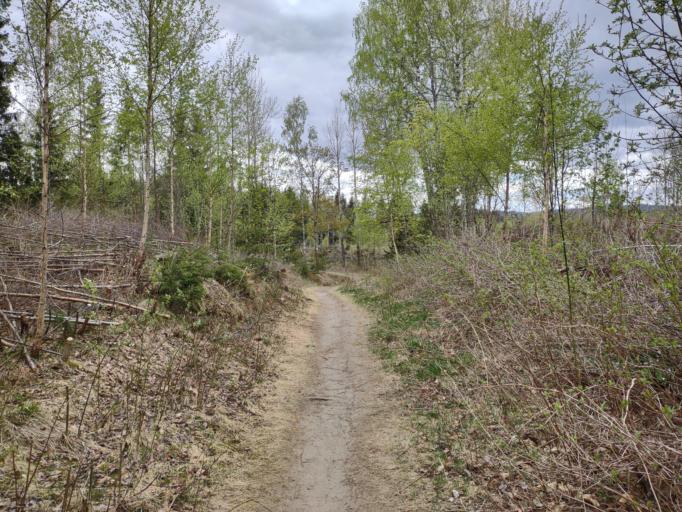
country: NO
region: Akershus
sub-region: Eidsvoll
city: Raholt
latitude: 60.2760
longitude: 11.1518
